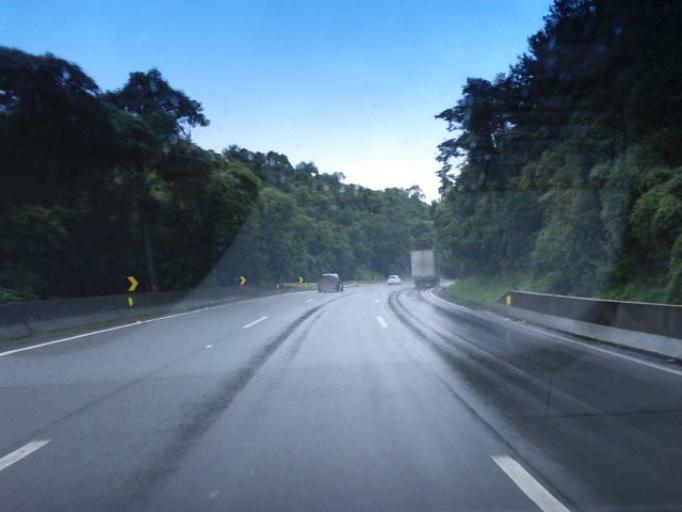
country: BR
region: Parana
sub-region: Sao Jose Dos Pinhais
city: Sao Jose dos Pinhais
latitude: -25.8423
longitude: -49.0337
